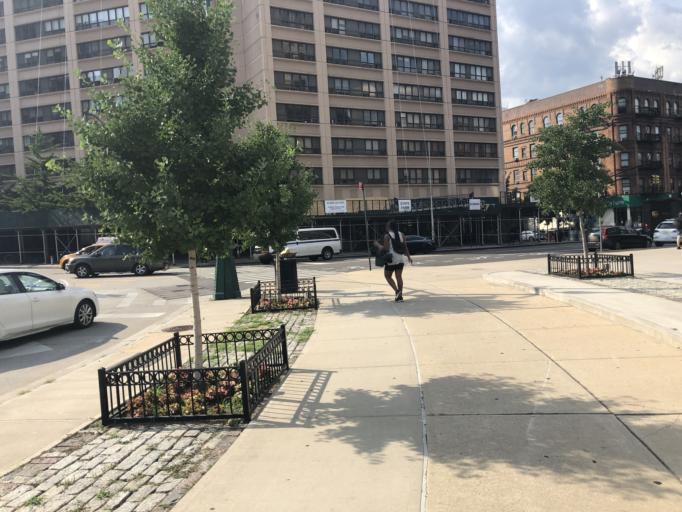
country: US
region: New York
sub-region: New York County
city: Manhattan
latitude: 40.8007
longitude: -73.9577
